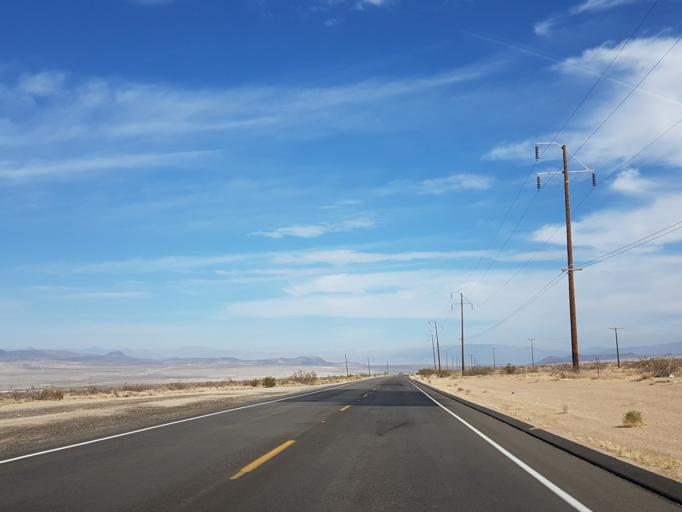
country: US
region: California
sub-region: Kern County
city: Ridgecrest
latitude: 35.6379
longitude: -117.5670
